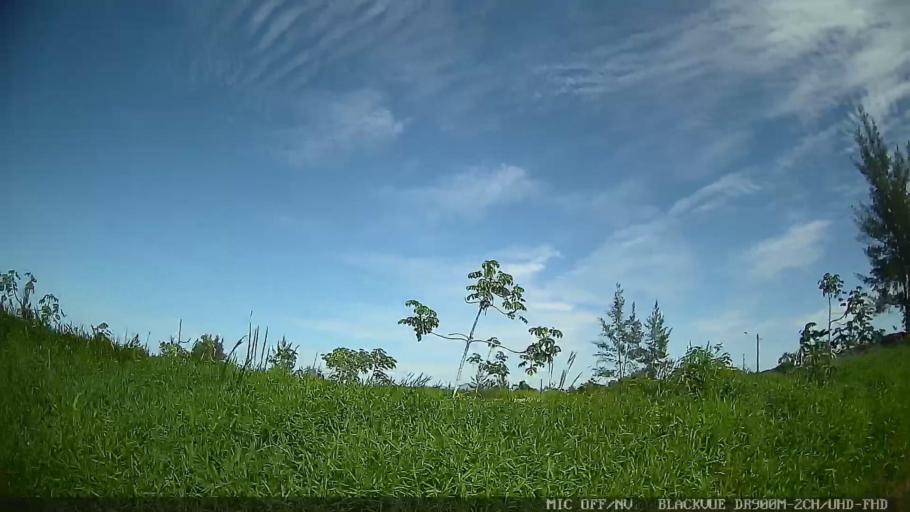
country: BR
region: Sao Paulo
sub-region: Iguape
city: Iguape
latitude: -24.7841
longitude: -47.6076
